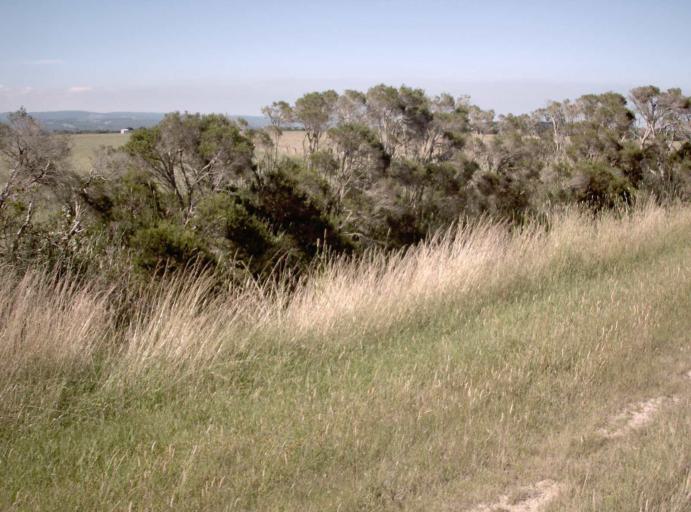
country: AU
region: Victoria
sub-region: Latrobe
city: Traralgon
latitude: -38.6284
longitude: 146.5994
